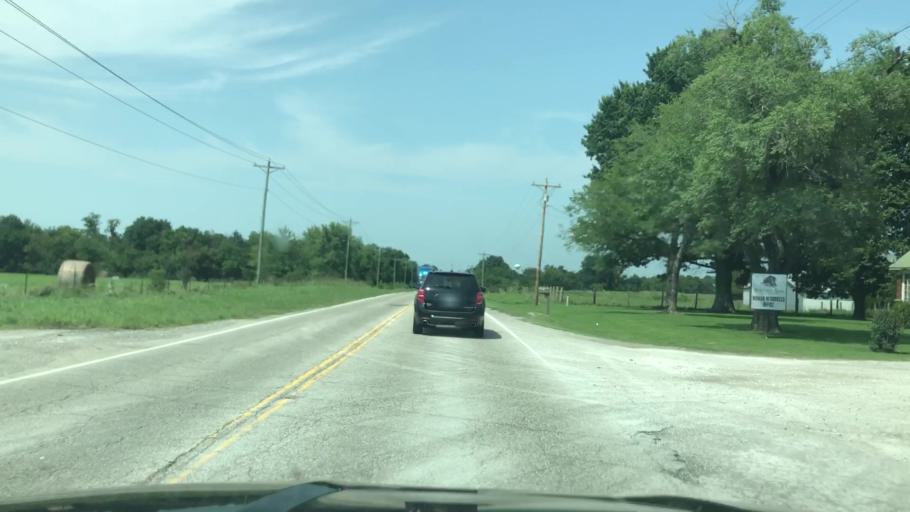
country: US
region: Oklahoma
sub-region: Ottawa County
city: Miami
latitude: 36.8928
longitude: -94.8418
